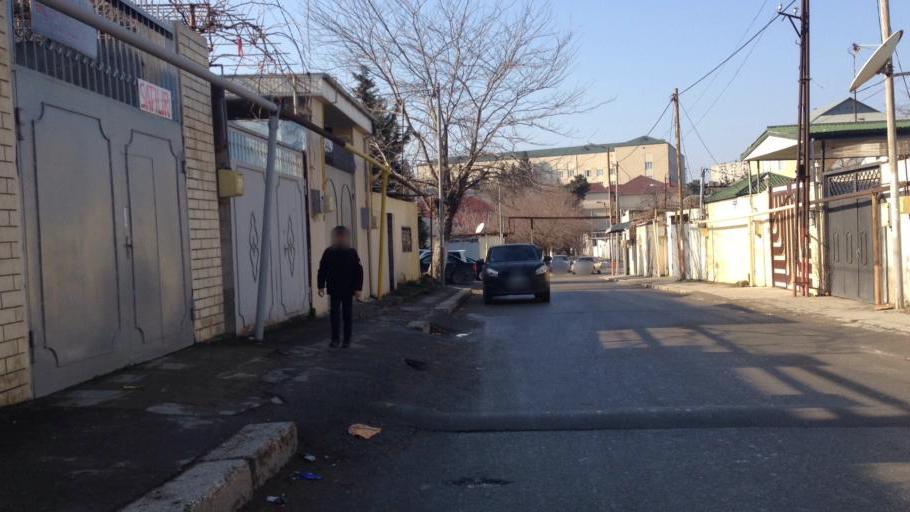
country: AZ
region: Baki
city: Binagadi
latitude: 40.4372
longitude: 49.8467
